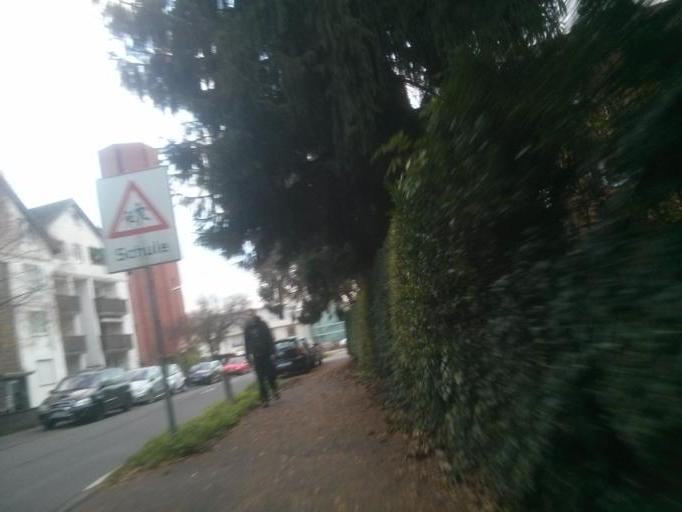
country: DE
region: North Rhine-Westphalia
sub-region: Regierungsbezirk Koln
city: Poll
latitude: 50.9203
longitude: 6.9898
